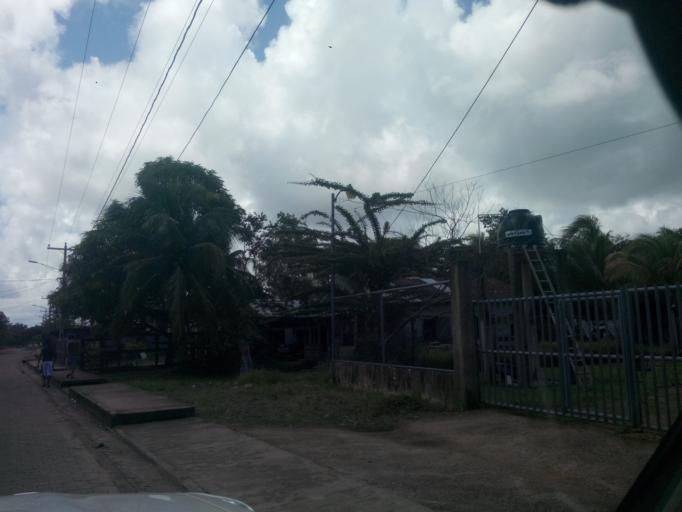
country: NI
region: Atlantico Norte (RAAN)
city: Puerto Cabezas
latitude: 14.0405
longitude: -83.3833
